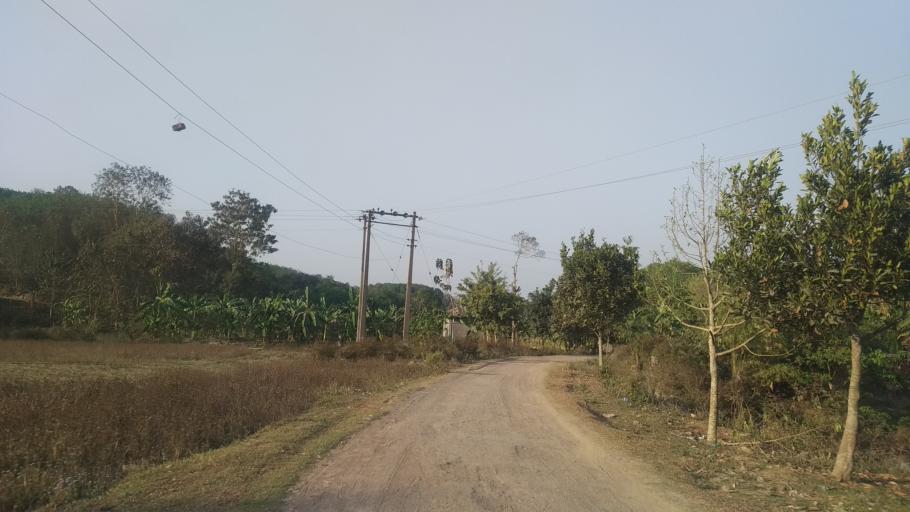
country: IN
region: Tripura
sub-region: West Tripura
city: Sonamura
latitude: 23.4414
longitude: 91.3628
